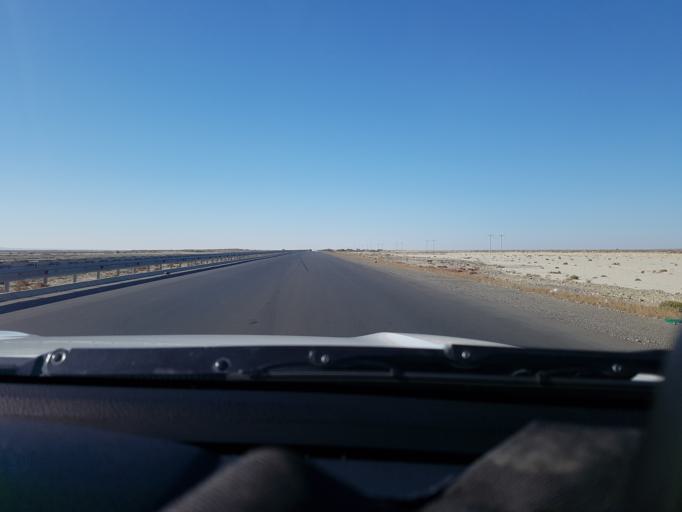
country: TM
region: Balkan
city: Gazanjyk
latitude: 39.2489
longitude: 55.0971
